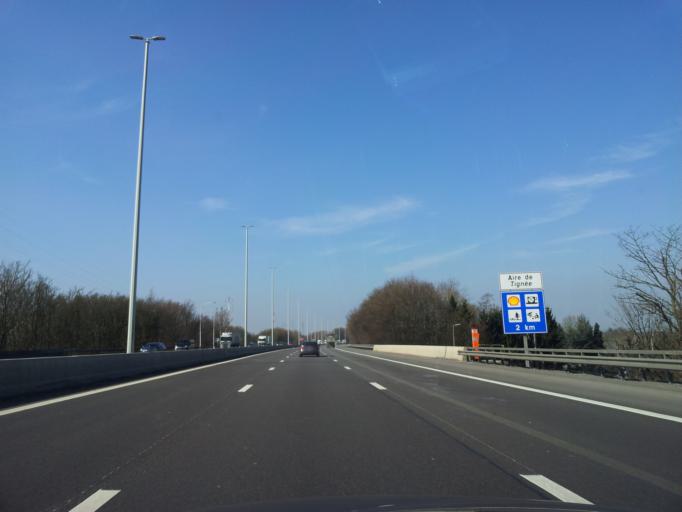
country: BE
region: Wallonia
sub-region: Province de Liege
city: Soumagne
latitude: 50.6394
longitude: 5.7350
